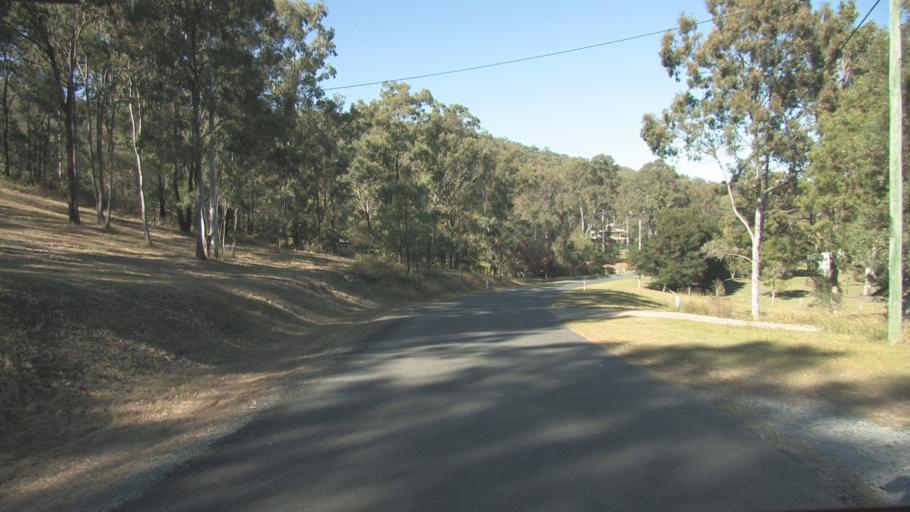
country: AU
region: Queensland
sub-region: Logan
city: Windaroo
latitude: -27.7795
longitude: 153.1480
